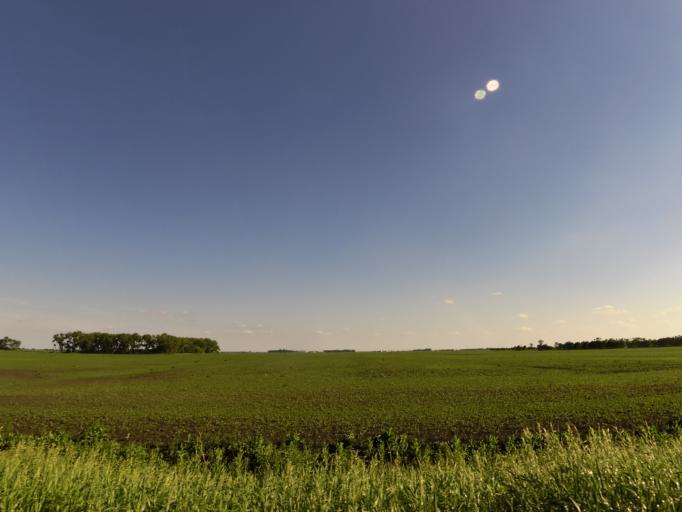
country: US
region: North Dakota
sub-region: Walsh County
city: Grafton
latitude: 48.3975
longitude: -97.2419
